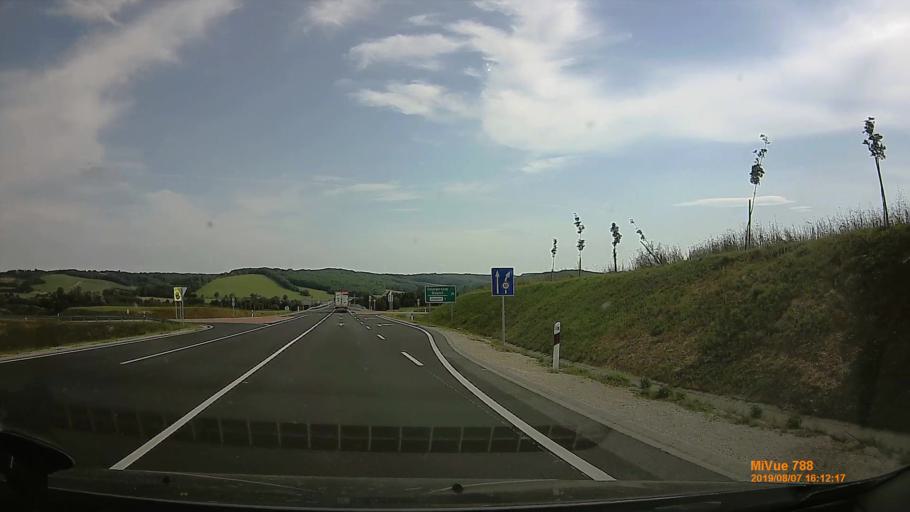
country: HU
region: Zala
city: Zalalovo
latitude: 46.8578
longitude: 16.6275
